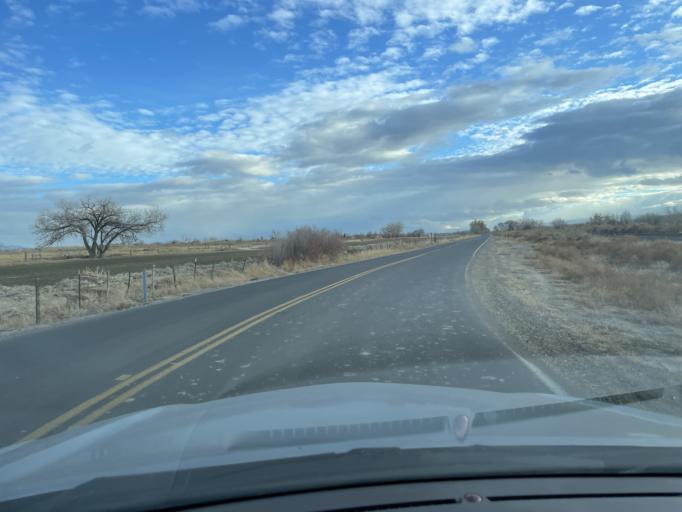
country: US
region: Colorado
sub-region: Montrose County
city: Olathe
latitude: 38.6424
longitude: -107.9933
